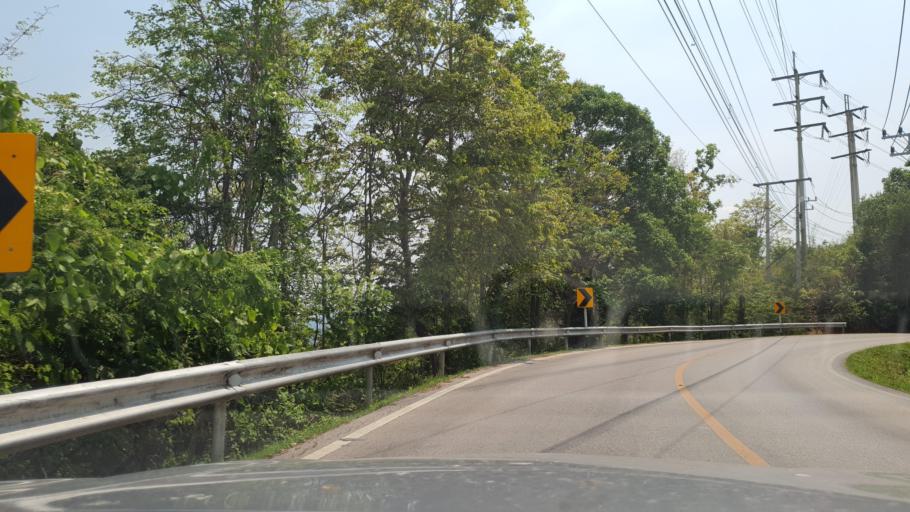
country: TH
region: Mae Hong Son
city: Mae Hi
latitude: 19.2698
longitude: 98.5394
